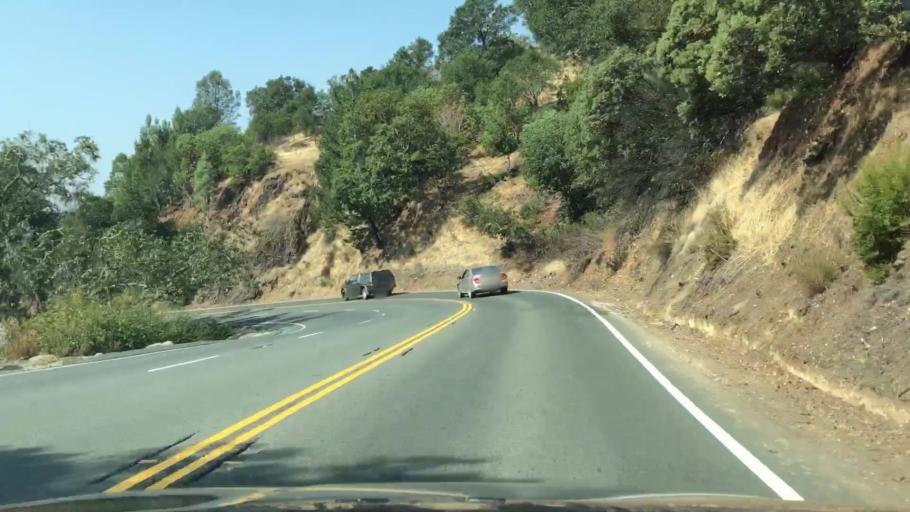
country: US
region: California
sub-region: Napa County
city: Calistoga
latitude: 38.6135
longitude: -122.5967
